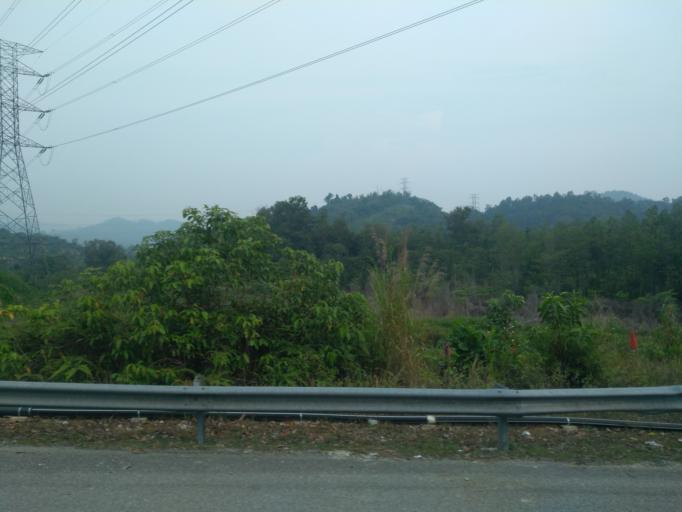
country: MY
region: Perak
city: Ipoh
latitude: 4.5542
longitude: 101.1662
